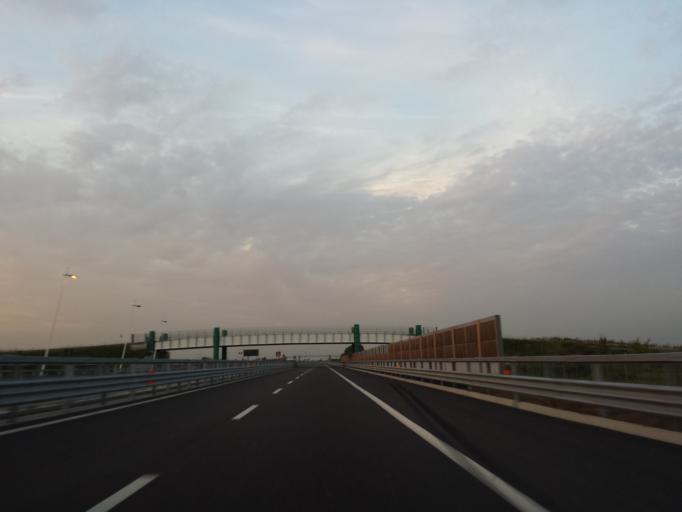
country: IT
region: Veneto
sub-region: Provincia di Vicenza
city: Villaganzerla
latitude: 45.4121
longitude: 11.6335
